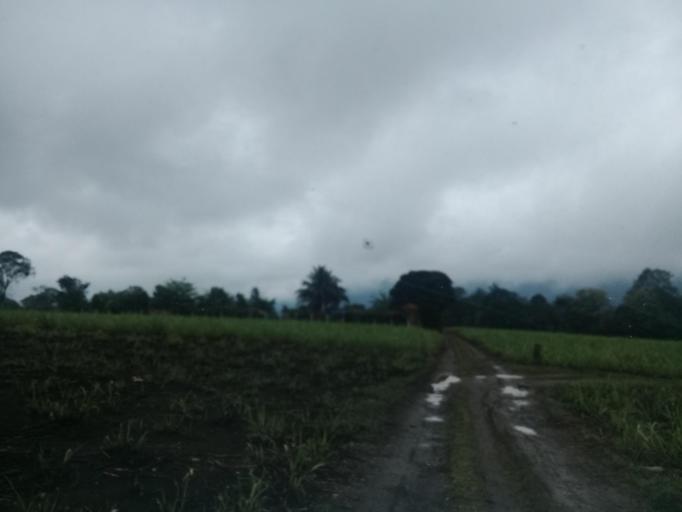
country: MX
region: Veracruz
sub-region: Amatlan de los Reyes
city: Centro de Readaptacion Social
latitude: 18.8216
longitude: -96.9544
